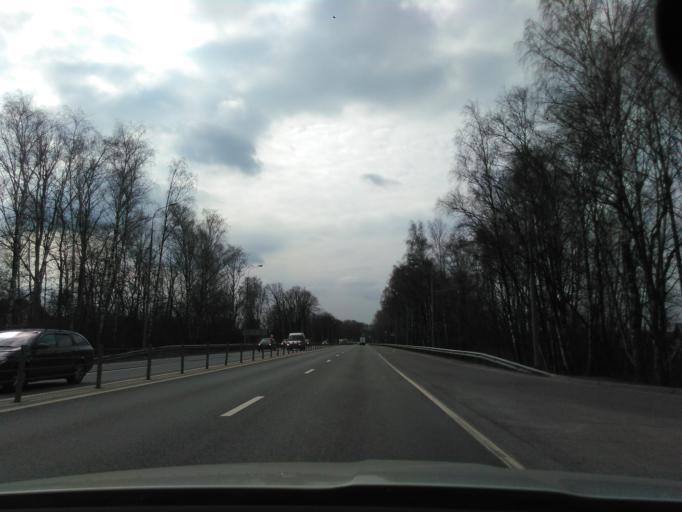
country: RU
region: Moskovskaya
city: Marfino
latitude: 56.0186
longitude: 37.5452
